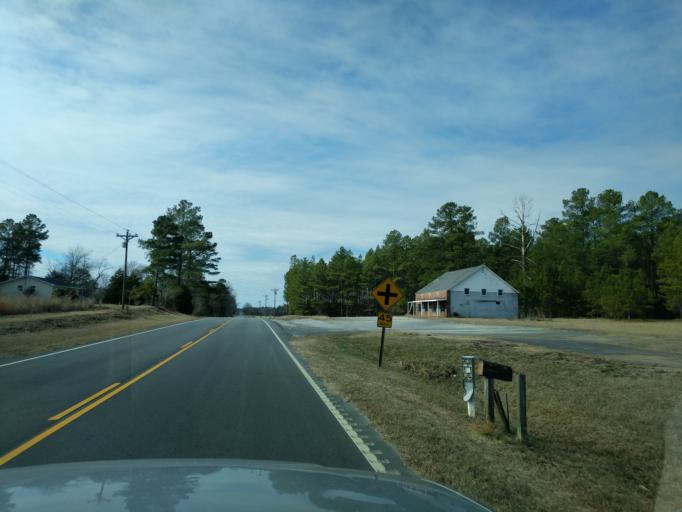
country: US
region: South Carolina
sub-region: Edgefield County
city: Edgefield
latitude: 33.9370
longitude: -81.9494
